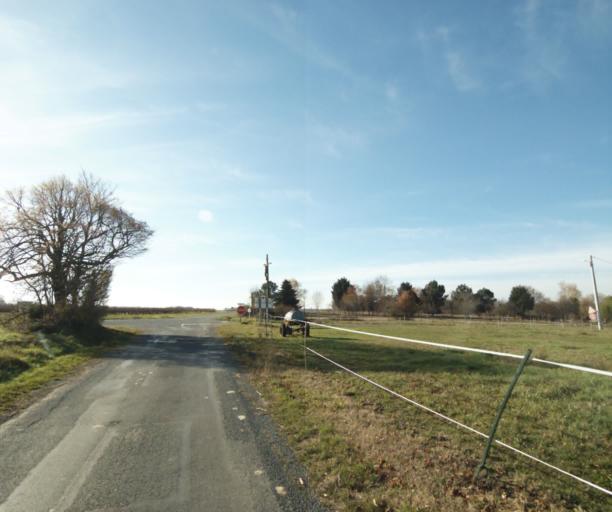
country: FR
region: Poitou-Charentes
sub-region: Departement de la Charente-Maritime
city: Chaniers
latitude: 45.7536
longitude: -0.5164
